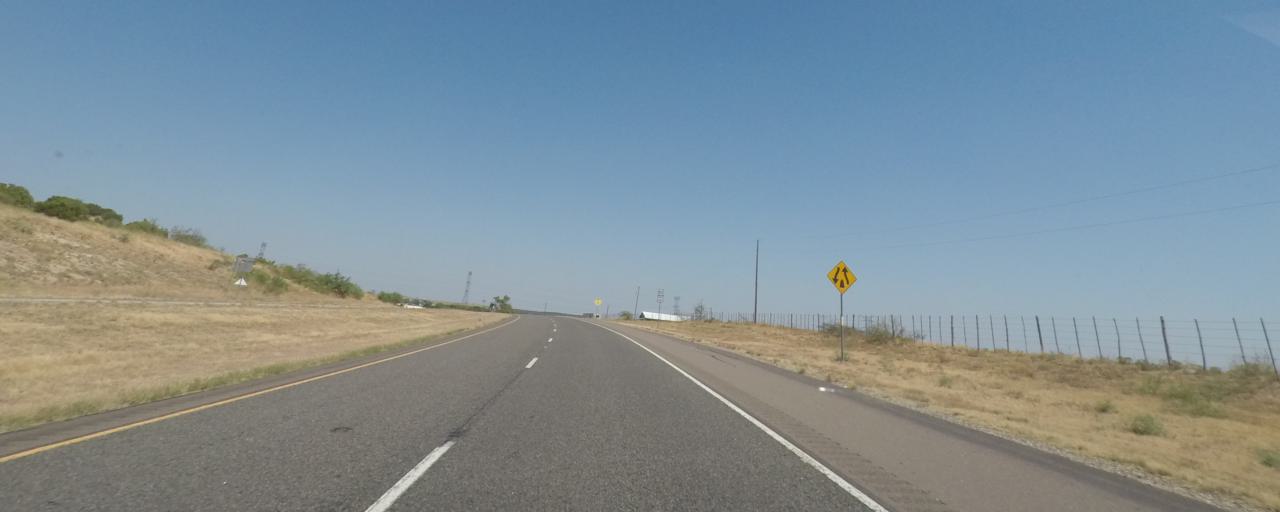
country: US
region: Texas
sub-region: Dickens County
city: Dickens
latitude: 33.6200
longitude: -100.8571
